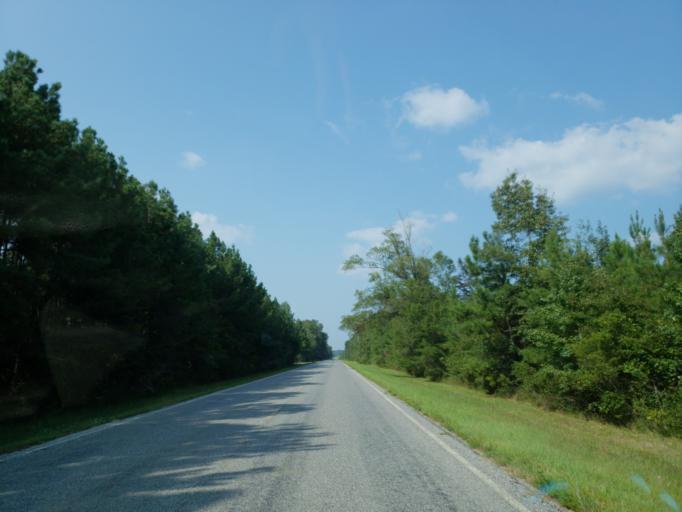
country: US
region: Mississippi
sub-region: Clarke County
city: Stonewall
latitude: 32.0247
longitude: -88.8889
